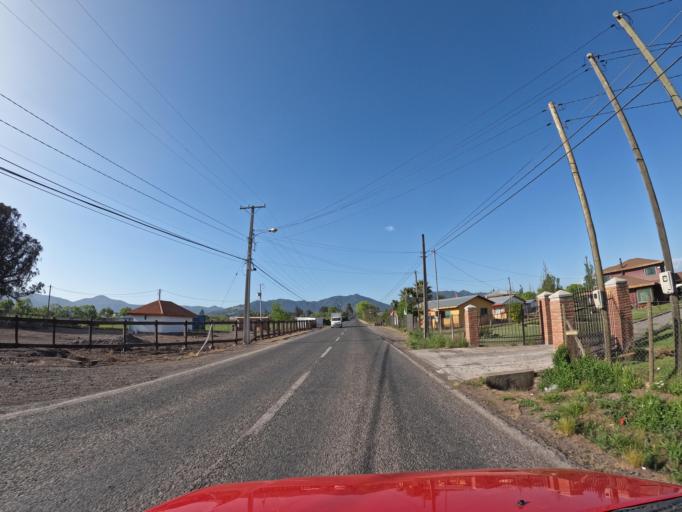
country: CL
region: Maule
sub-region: Provincia de Curico
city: Rauco
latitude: -34.8776
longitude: -71.2685
